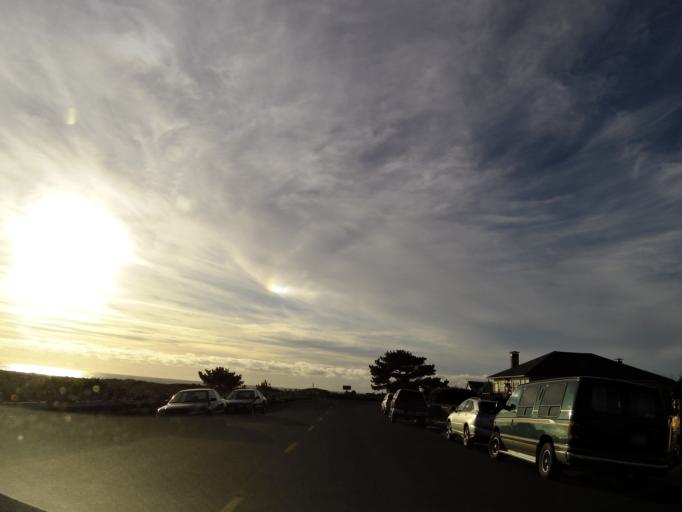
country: US
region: California
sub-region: Mendocino County
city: Fort Bragg
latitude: 39.3043
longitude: -123.8035
